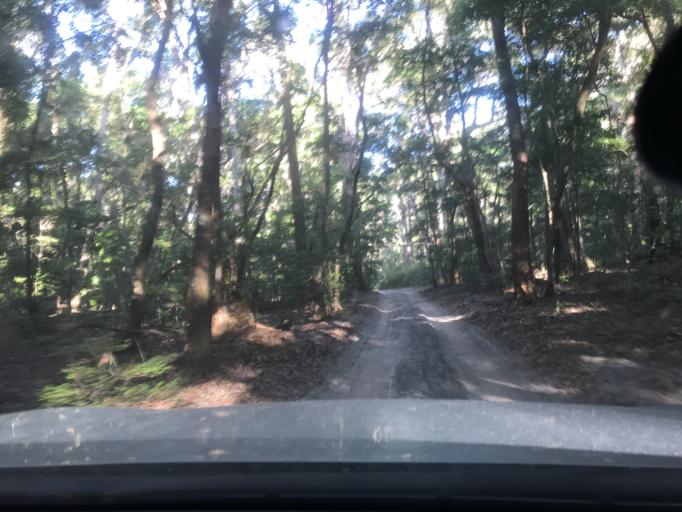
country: AU
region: Queensland
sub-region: Fraser Coast
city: Urangan
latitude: -25.3264
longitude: 153.1507
